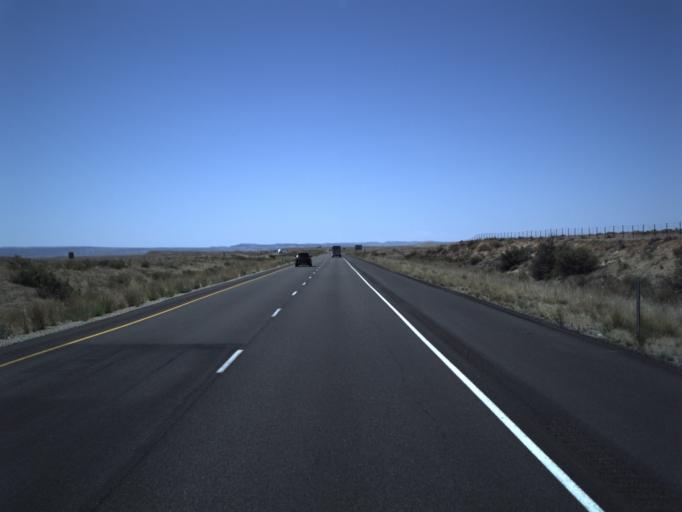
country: US
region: Colorado
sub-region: Mesa County
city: Loma
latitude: 39.0459
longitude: -109.2729
